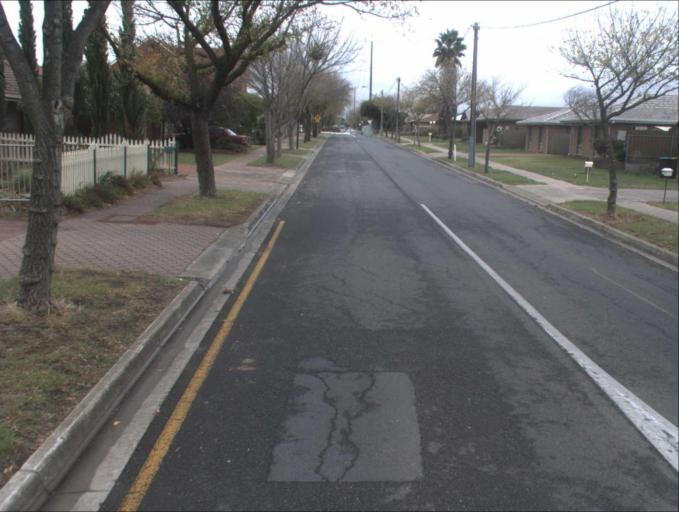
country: AU
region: South Australia
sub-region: Port Adelaide Enfield
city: Gilles Plains
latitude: -34.8590
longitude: 138.6364
